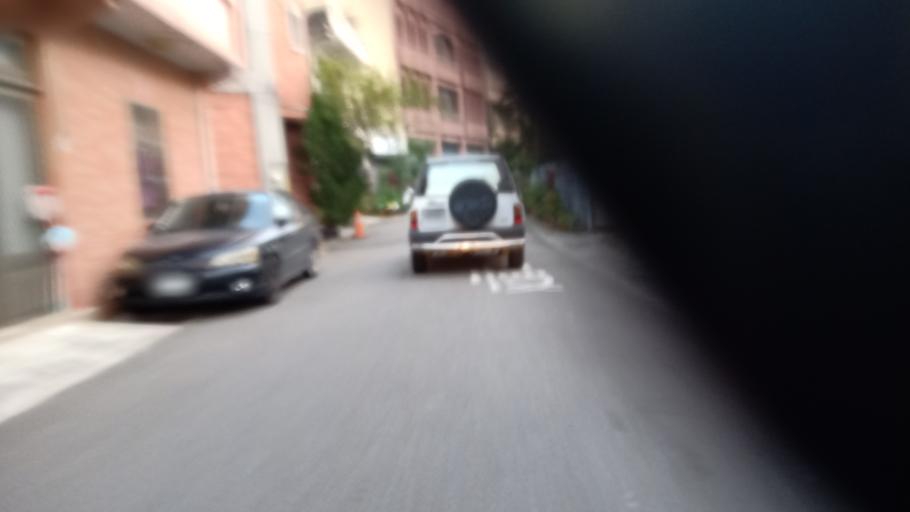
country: TW
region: Taiwan
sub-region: Hsinchu
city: Hsinchu
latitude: 24.7093
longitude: 120.9222
